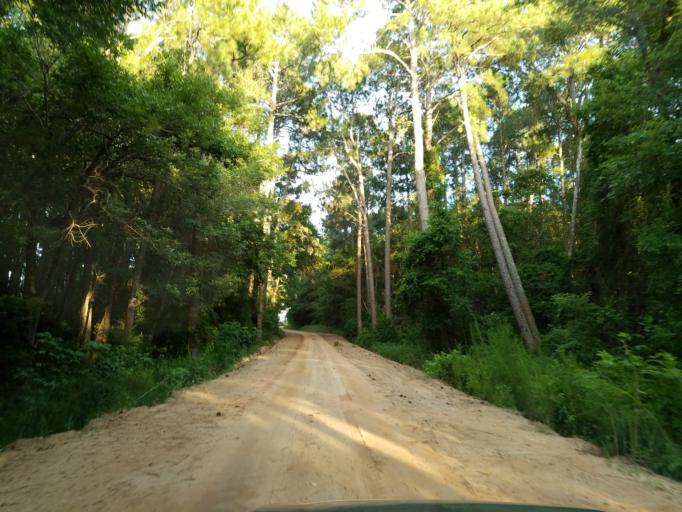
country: US
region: Georgia
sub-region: Turner County
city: Ashburn
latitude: 31.6385
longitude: -83.5874
